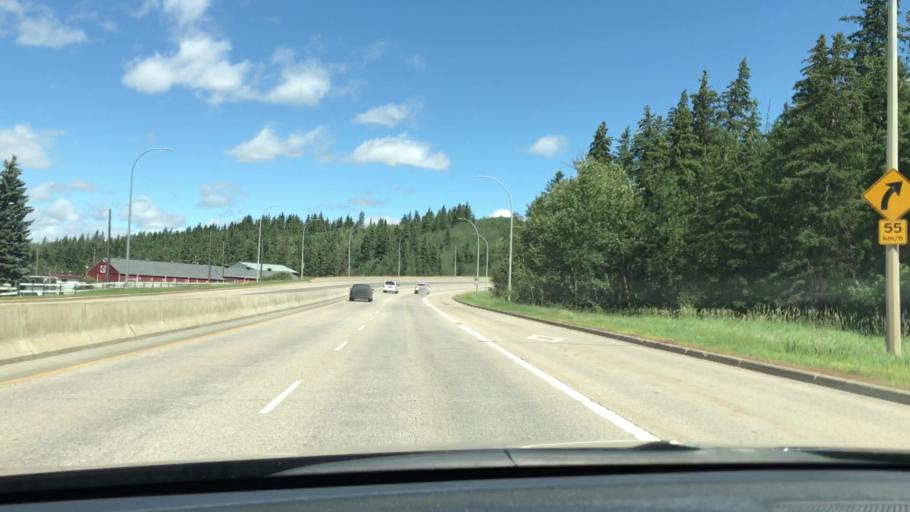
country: CA
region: Alberta
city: Edmonton
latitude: 53.5048
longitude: -113.5477
